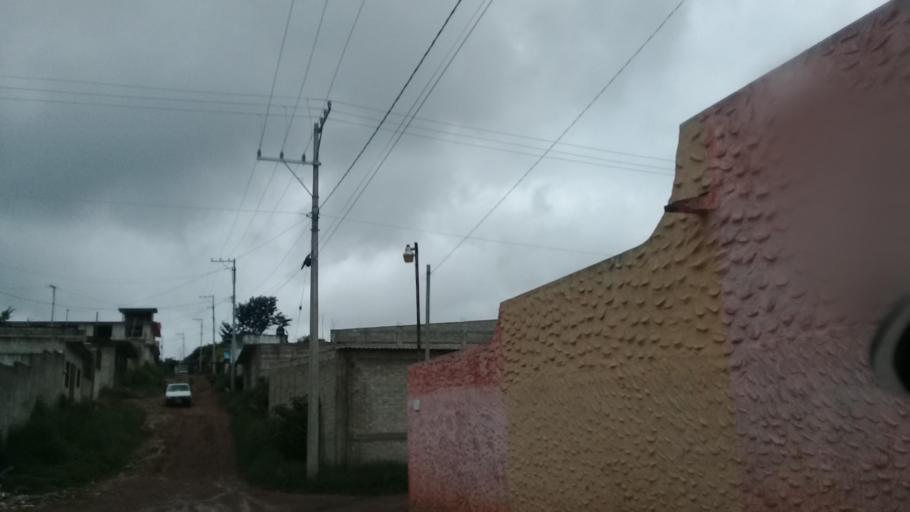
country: MX
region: Veracruz
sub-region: Emiliano Zapata
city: Las Trancas
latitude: 19.4968
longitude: -96.8638
